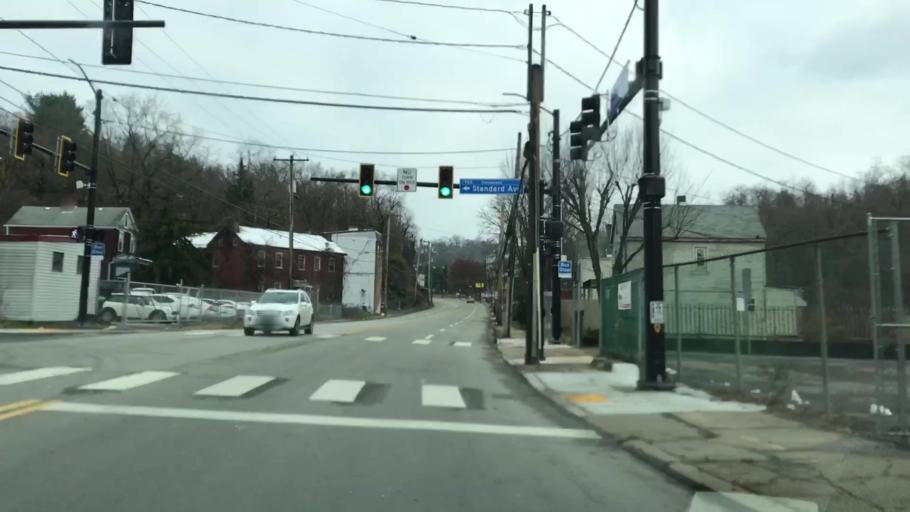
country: US
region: Pennsylvania
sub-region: Allegheny County
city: Wilkinsburg
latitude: 40.4570
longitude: -79.8778
